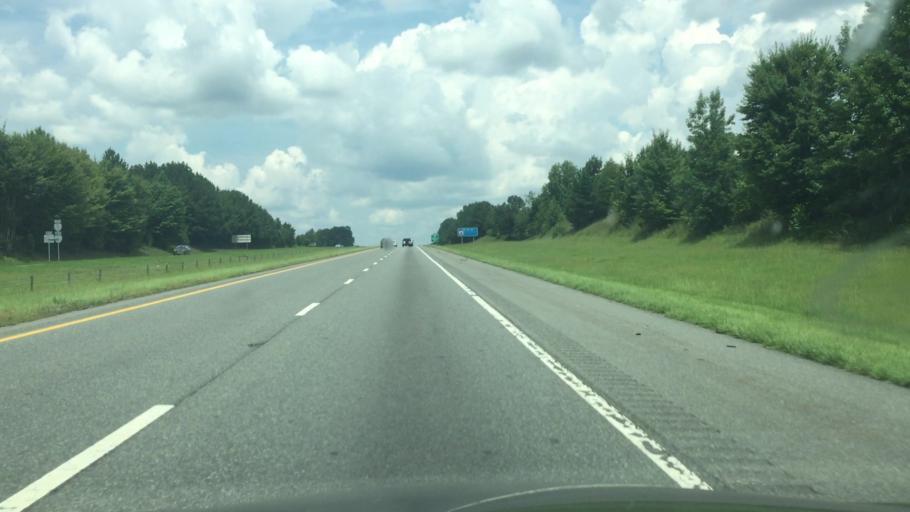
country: US
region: North Carolina
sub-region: Montgomery County
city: Biscoe
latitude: 35.5278
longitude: -79.7864
